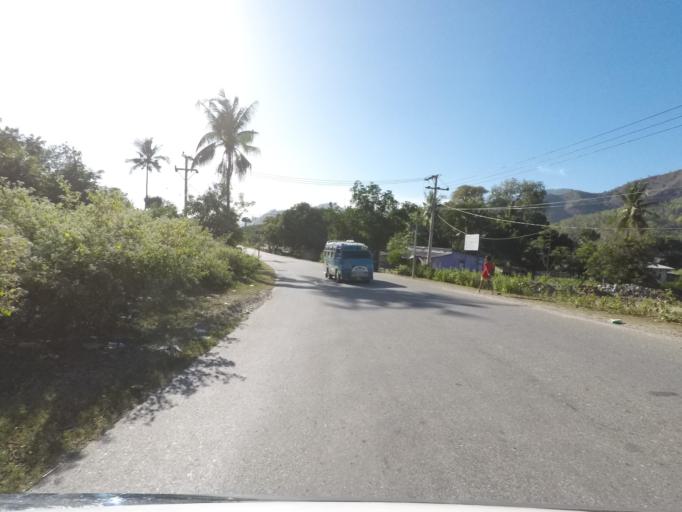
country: TL
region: Dili
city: Dili
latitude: -8.5578
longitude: 125.6455
